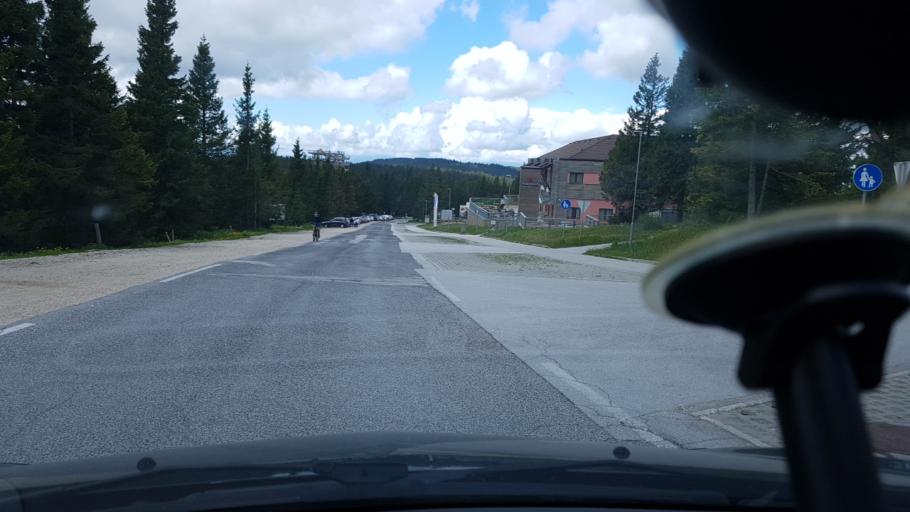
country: SI
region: Mislinja
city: Mislinja
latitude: 46.4524
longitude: 15.3310
